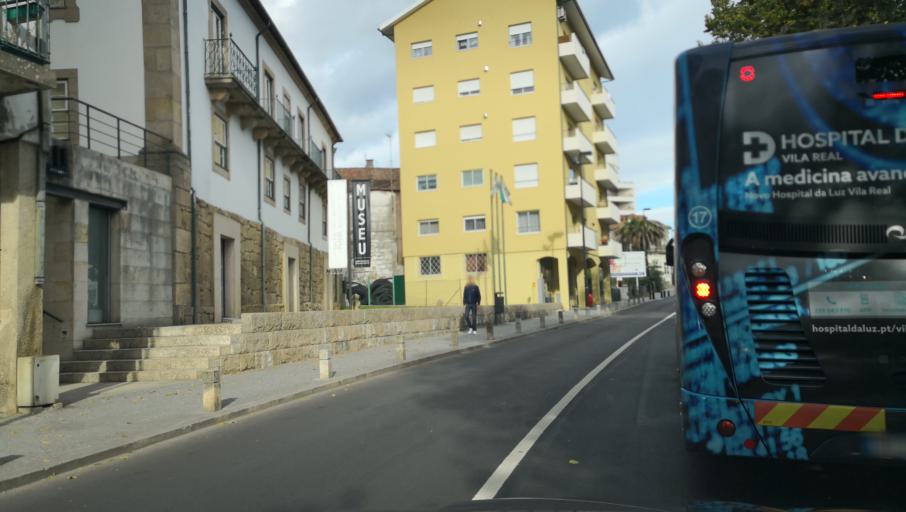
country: PT
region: Vila Real
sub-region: Vila Real
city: Vila Real
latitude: 41.2974
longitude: -7.7433
